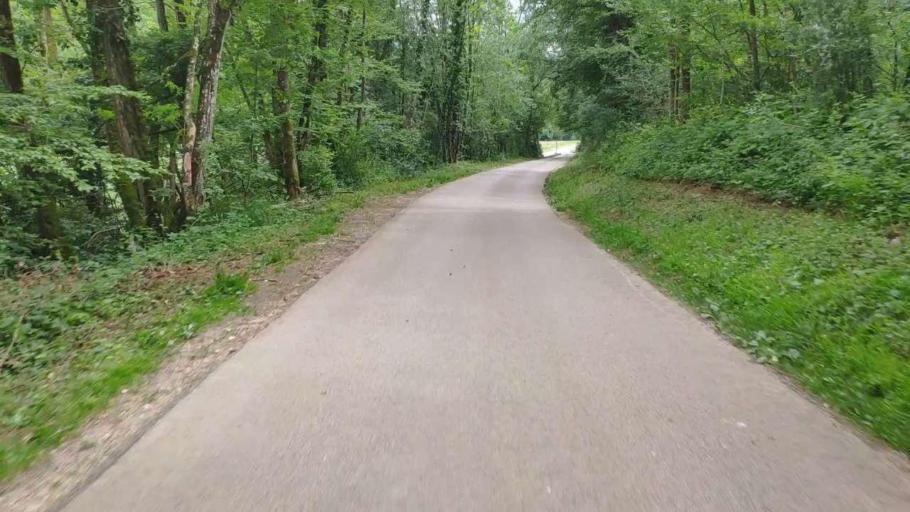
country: FR
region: Franche-Comte
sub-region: Departement du Jura
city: Montmorot
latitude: 46.7431
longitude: 5.5320
